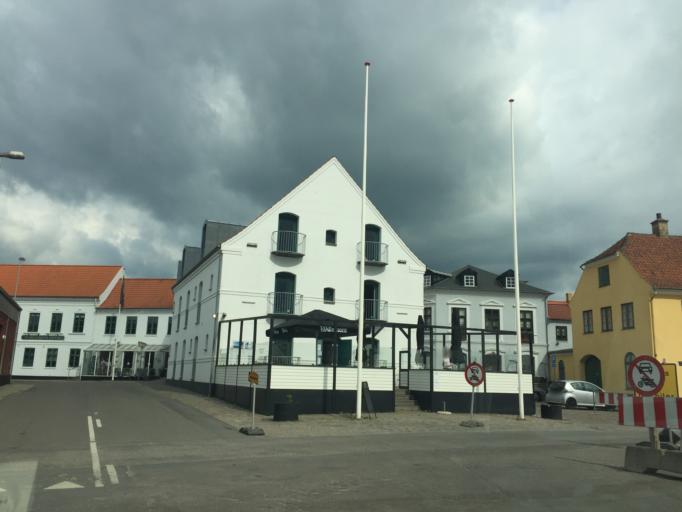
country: DK
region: South Denmark
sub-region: Assens Kommune
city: Assens
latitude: 55.2708
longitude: 9.8899
